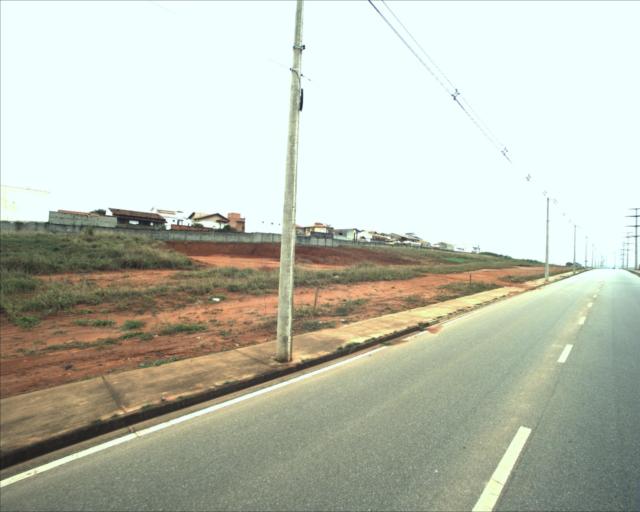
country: BR
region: Sao Paulo
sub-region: Sorocaba
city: Sorocaba
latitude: -23.4467
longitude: -47.4546
